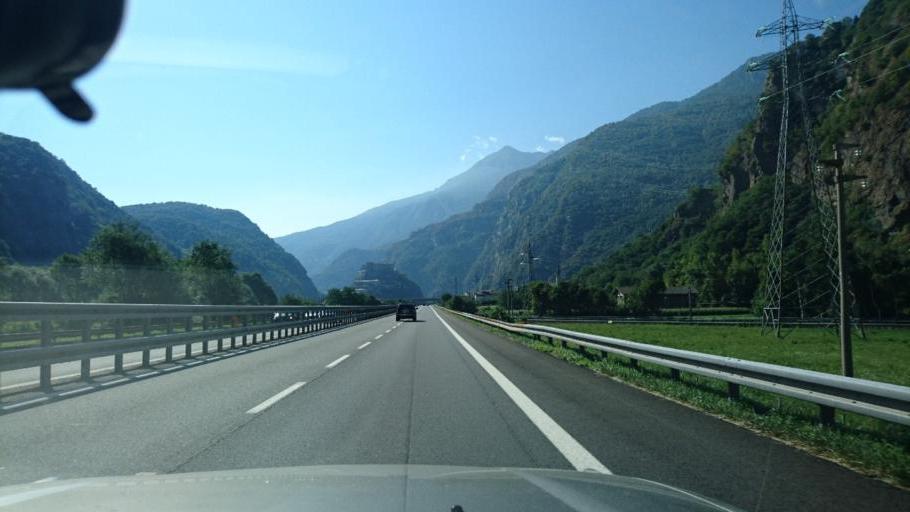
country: IT
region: Aosta Valley
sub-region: Valle d'Aosta
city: Hone
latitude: 45.6206
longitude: 7.7343
